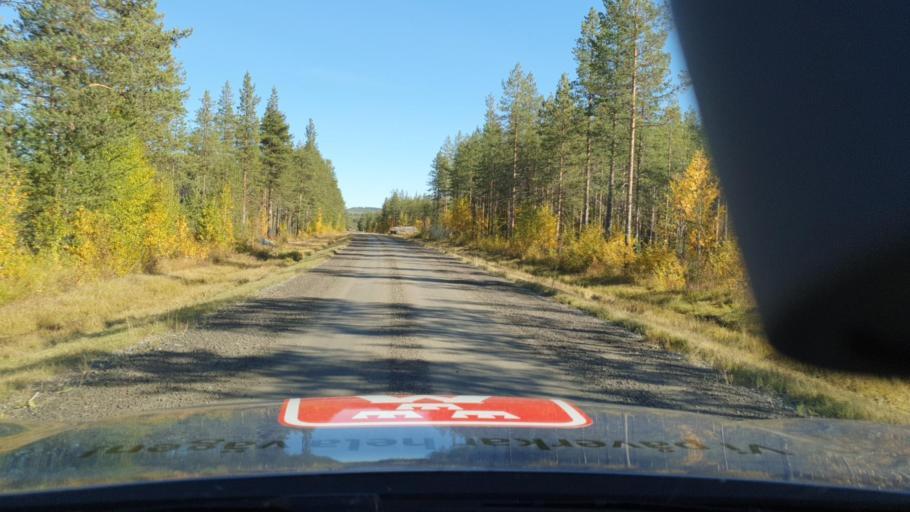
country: SE
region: Norrbotten
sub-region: Bodens Kommun
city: Boden
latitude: 66.0603
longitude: 21.3845
